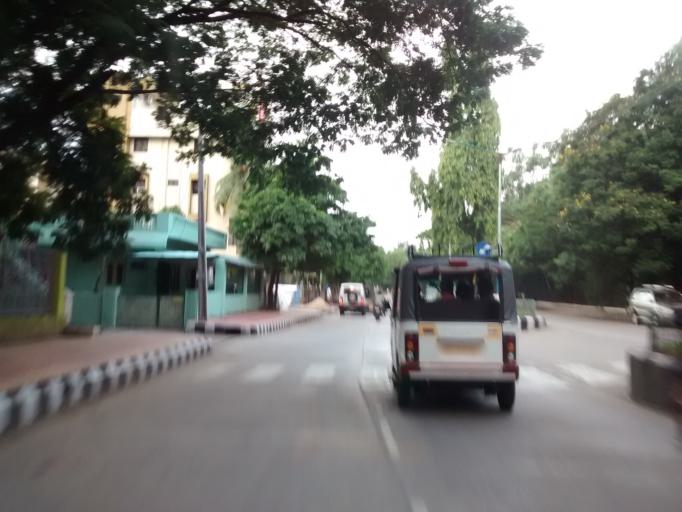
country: IN
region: Andhra Pradesh
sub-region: Chittoor
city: Akkarampalle
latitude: 13.6527
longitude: 79.4187
